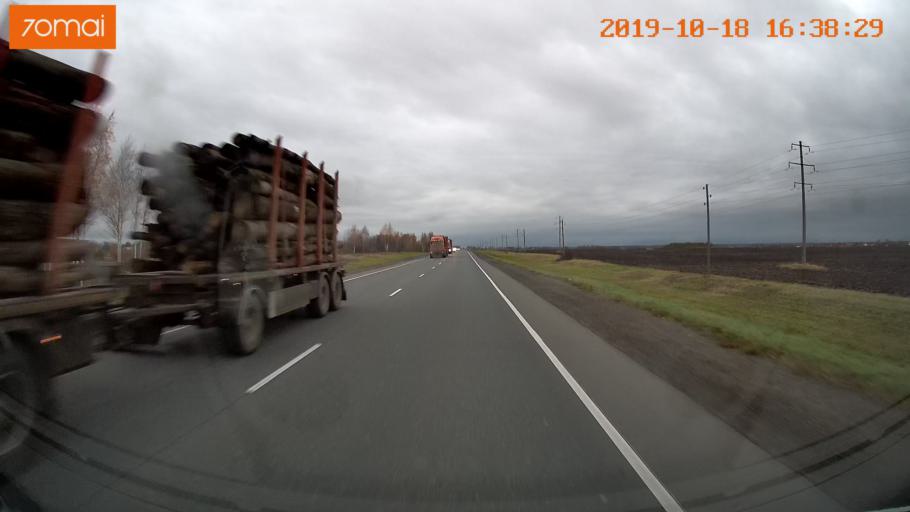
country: RU
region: Vladimir
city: Suzdal'
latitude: 56.4371
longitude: 40.4689
